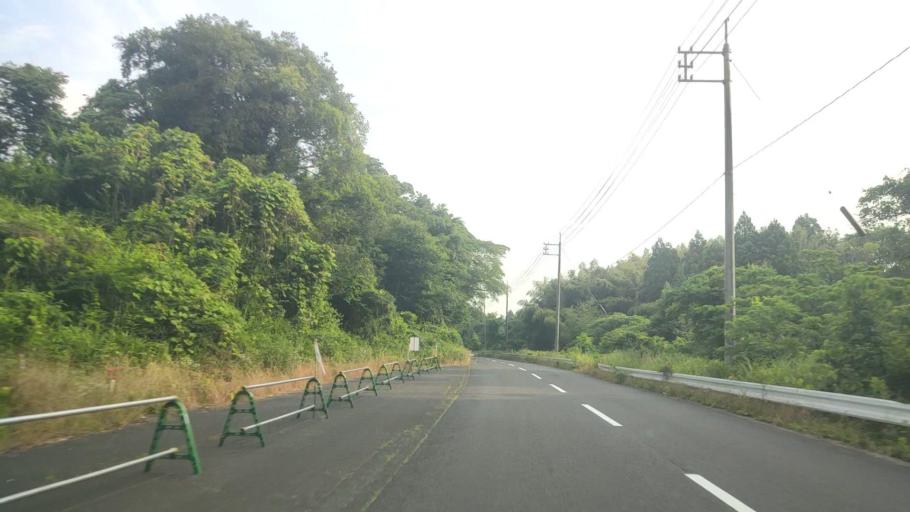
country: JP
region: Tottori
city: Kurayoshi
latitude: 35.4104
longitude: 133.7814
